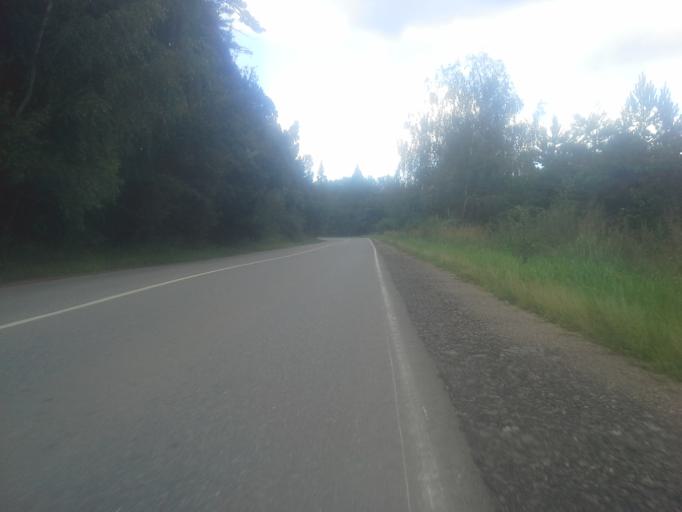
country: RU
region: Moskovskaya
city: Karinskoye
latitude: 55.6653
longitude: 36.6467
